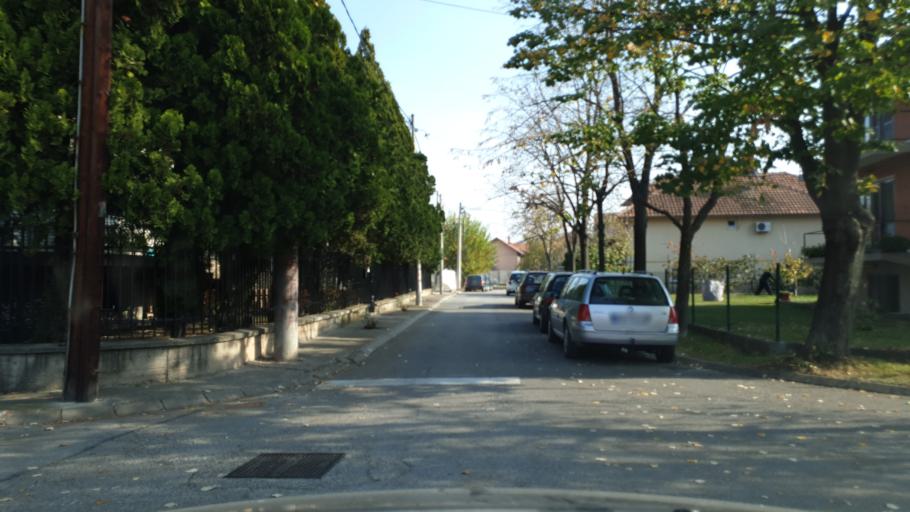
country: RS
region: Central Serbia
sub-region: Pomoravski Okrug
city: Paracin
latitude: 43.8587
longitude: 21.4258
